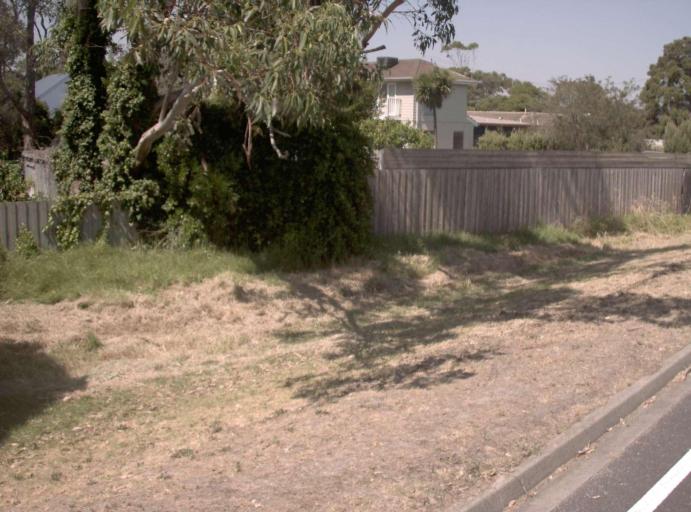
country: AU
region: Victoria
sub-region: Frankston
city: Seaford
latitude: -38.1096
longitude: 145.1351
